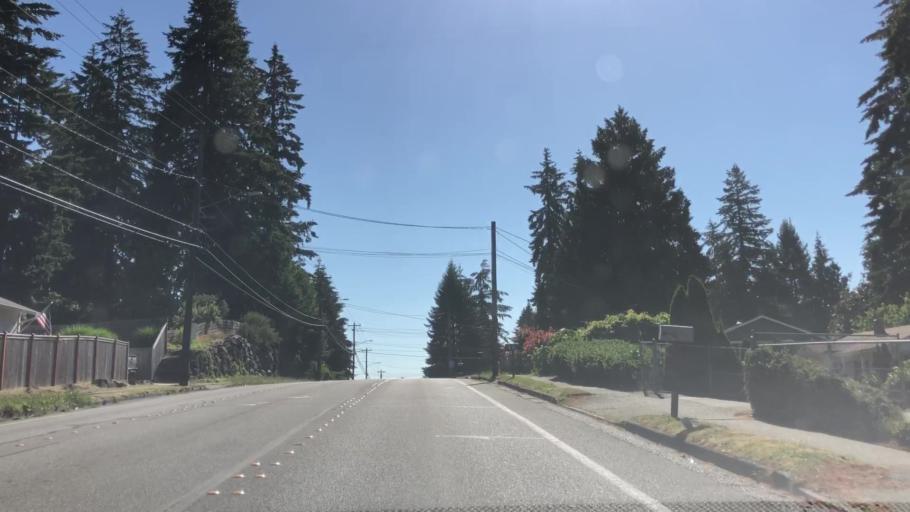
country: US
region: Washington
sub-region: Snohomish County
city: Lynnwood
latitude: 47.8175
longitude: -122.3078
